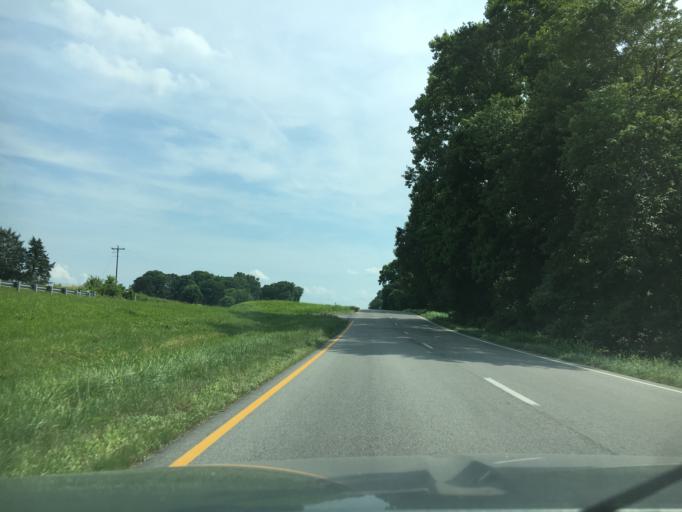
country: US
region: Virginia
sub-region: Nottoway County
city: Crewe
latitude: 37.2565
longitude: -78.1393
